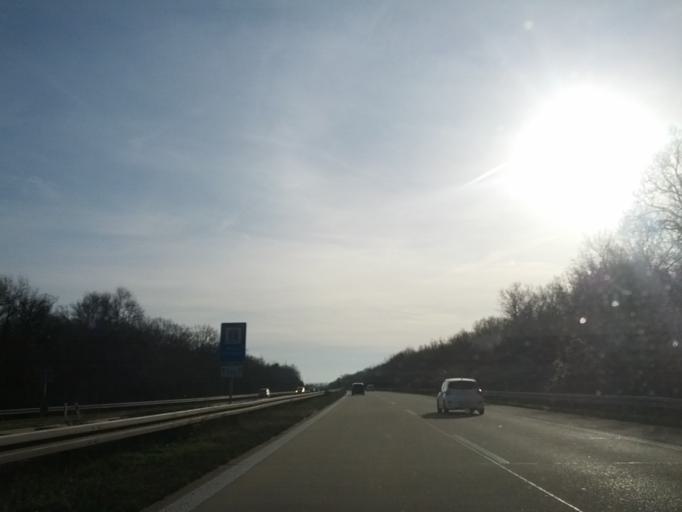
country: DE
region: Bavaria
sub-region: Regierungsbezirk Unterfranken
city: Sulzfeld am Main
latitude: 49.7004
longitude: 10.1076
